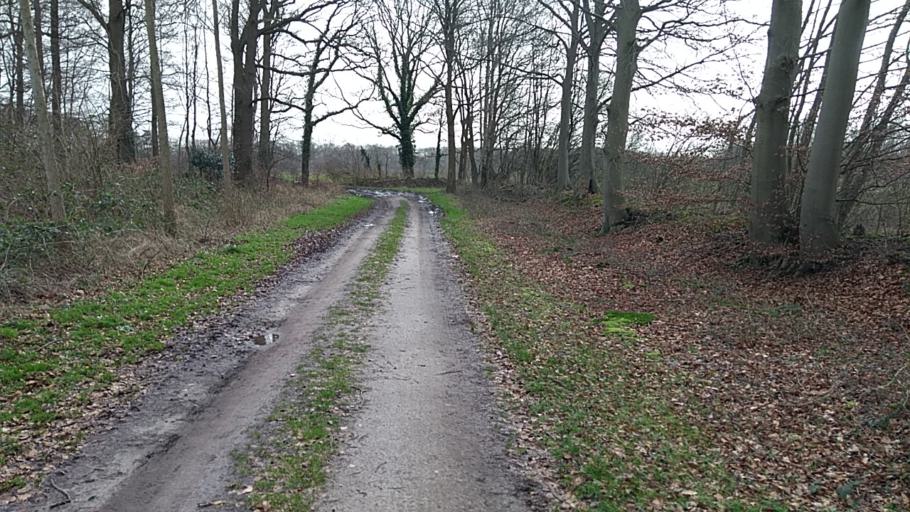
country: NL
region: Overijssel
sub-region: Gemeente Deventer
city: Schalkhaar
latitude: 52.2611
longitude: 6.2435
